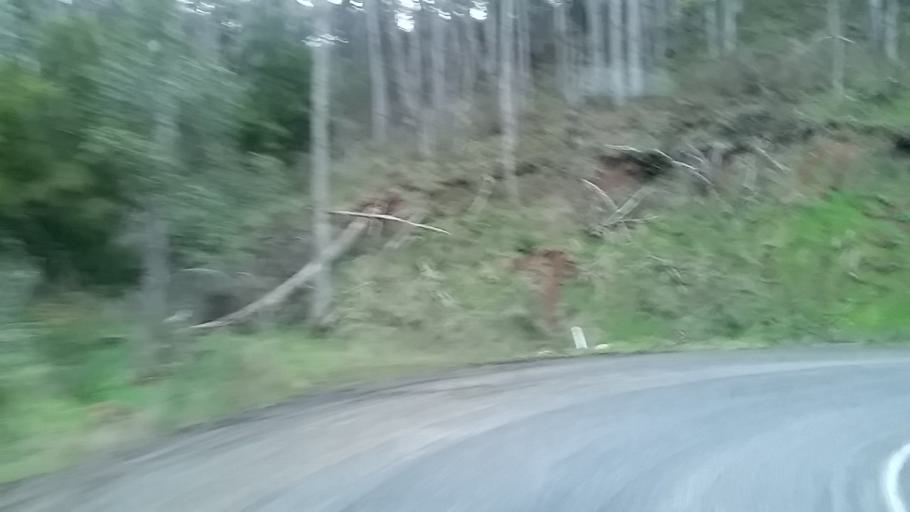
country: AU
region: South Australia
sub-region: Adelaide Hills
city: Lobethal
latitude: -34.8889
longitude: 138.8372
